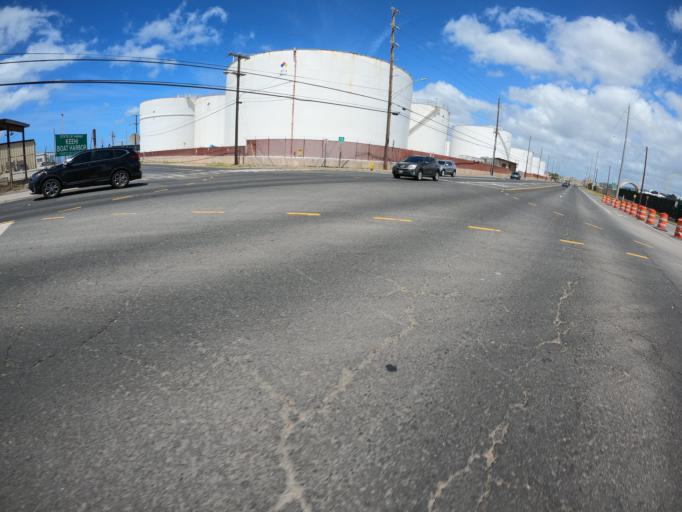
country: US
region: Hawaii
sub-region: Honolulu County
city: Honolulu
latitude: 21.3169
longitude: -157.8887
